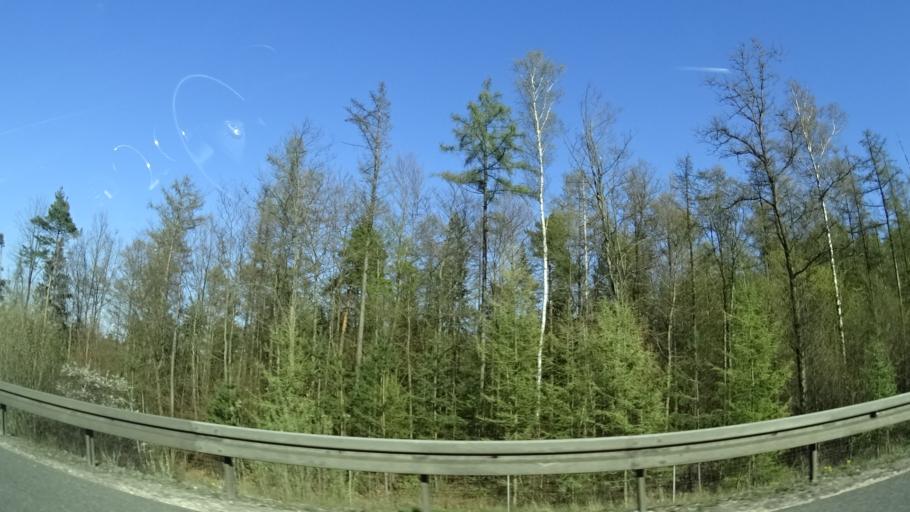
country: DE
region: Bavaria
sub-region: Upper Franconia
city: Haag
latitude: 49.8889
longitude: 11.5982
